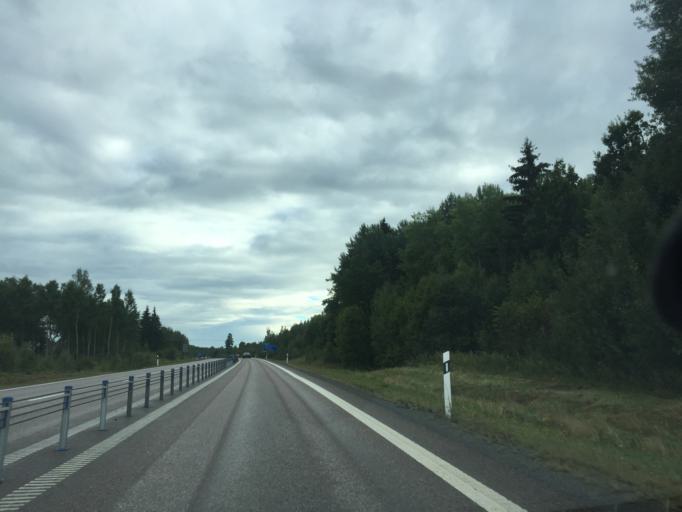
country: SE
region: Vaestmanland
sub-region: Arboga Kommun
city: Arboga
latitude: 59.4186
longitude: 15.8857
